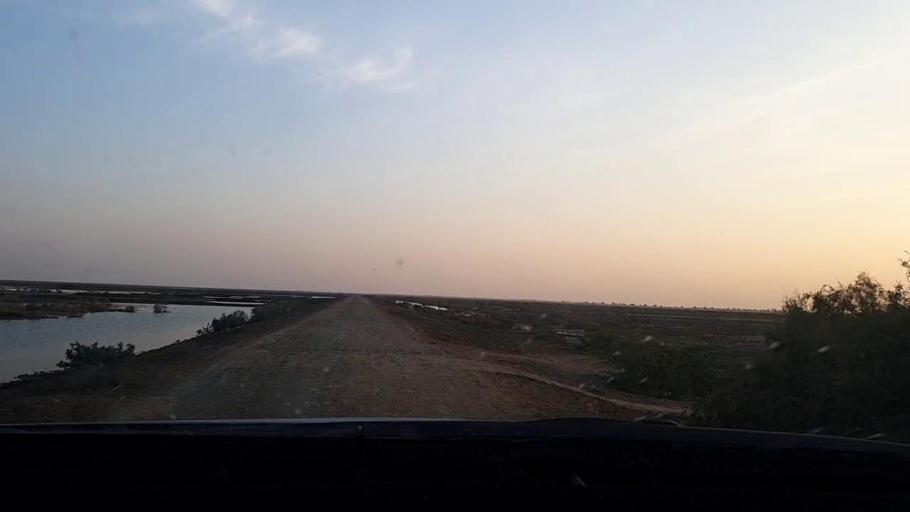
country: PK
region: Sindh
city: Tando Mittha Khan
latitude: 25.8477
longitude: 69.2304
